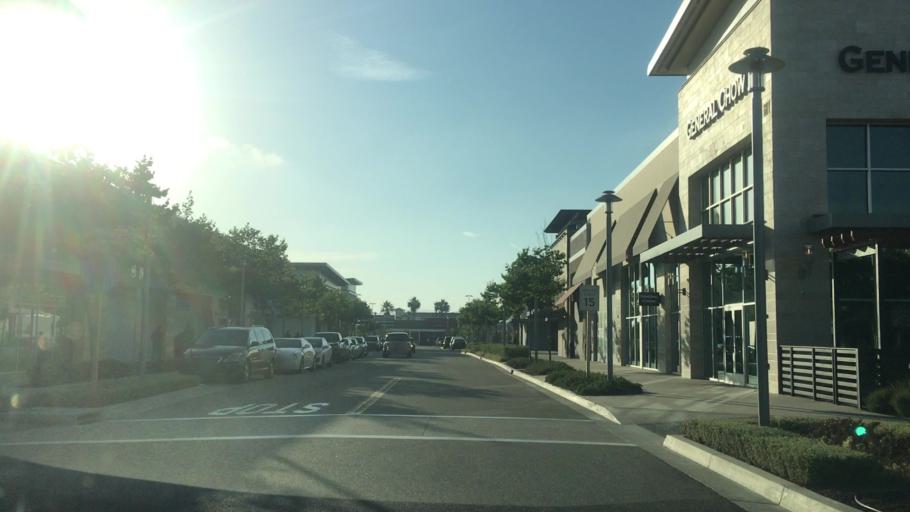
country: US
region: California
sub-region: Ventura County
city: El Rio
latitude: 34.2408
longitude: -119.1770
